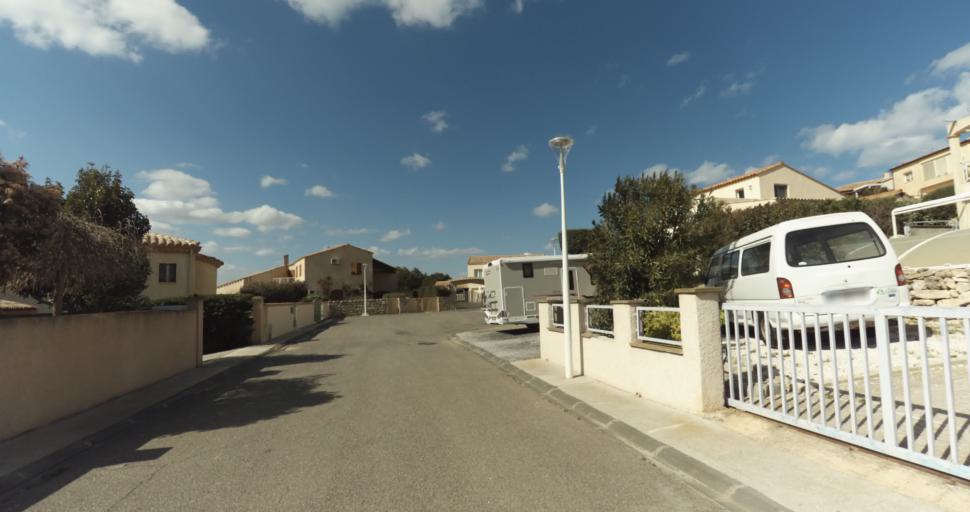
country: FR
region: Languedoc-Roussillon
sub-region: Departement de l'Aude
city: Leucate
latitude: 42.9062
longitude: 3.0464
